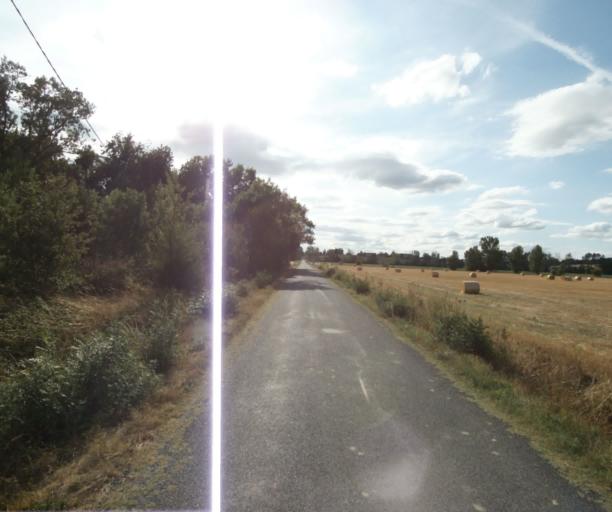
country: FR
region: Midi-Pyrenees
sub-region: Departement du Tarn
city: Puylaurens
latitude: 43.5194
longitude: 1.9995
